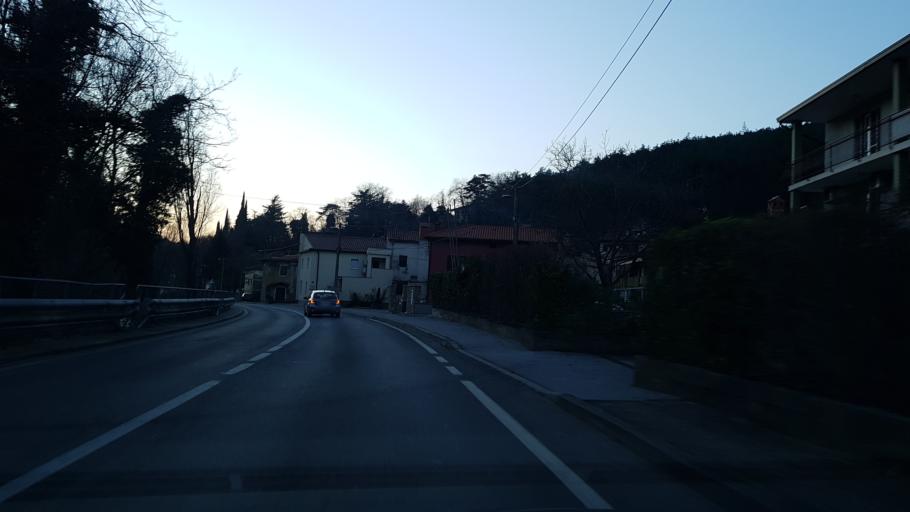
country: SI
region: Koper-Capodistria
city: Sv. Anton
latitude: 45.5445
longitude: 13.8457
